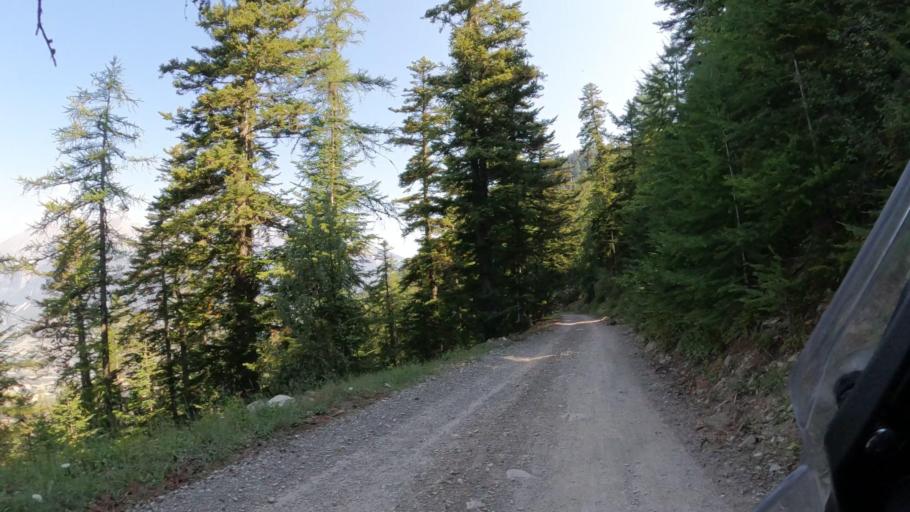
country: FR
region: Provence-Alpes-Cote d'Azur
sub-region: Departement des Hautes-Alpes
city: Embrun
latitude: 44.5907
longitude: 6.5653
